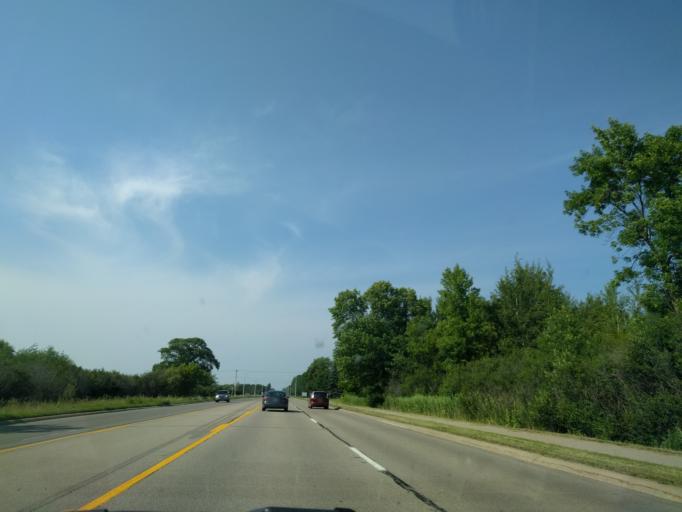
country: US
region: Michigan
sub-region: Delta County
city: Escanaba
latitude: 45.7227
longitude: -87.0801
